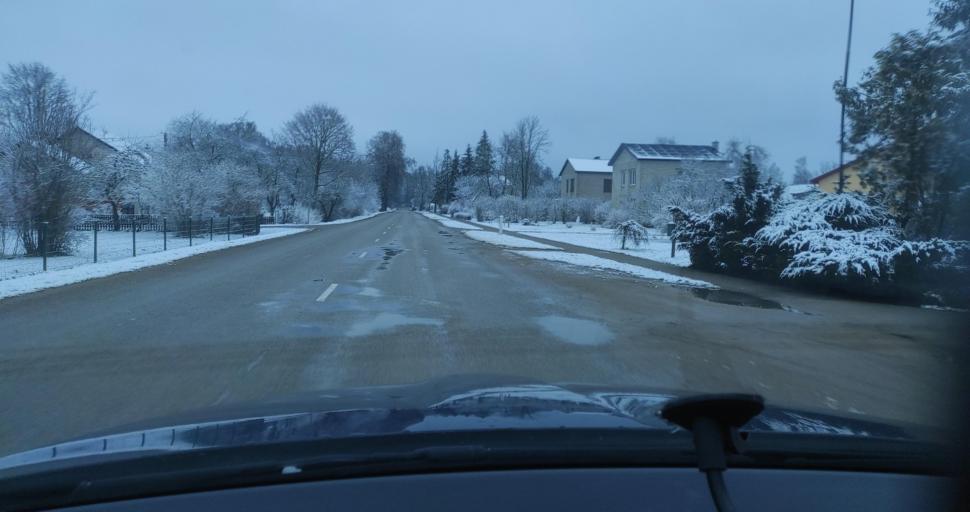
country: LV
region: Skrunda
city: Skrunda
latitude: 56.8695
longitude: 22.2343
